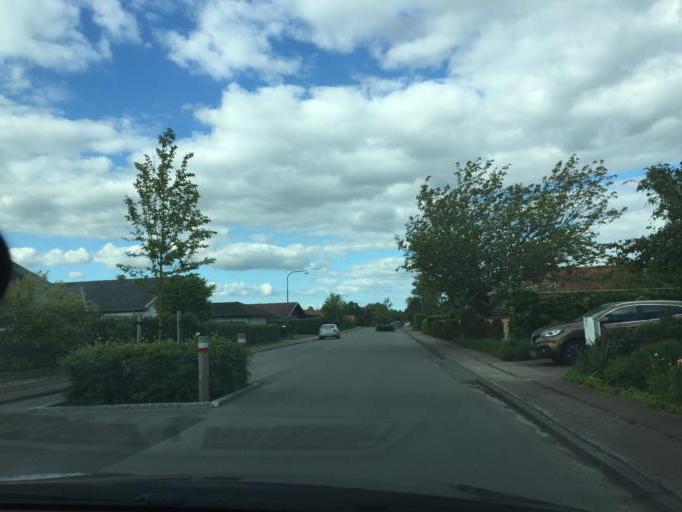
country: DK
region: South Denmark
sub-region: Odense Kommune
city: Bellinge
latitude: 55.3499
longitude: 10.3475
